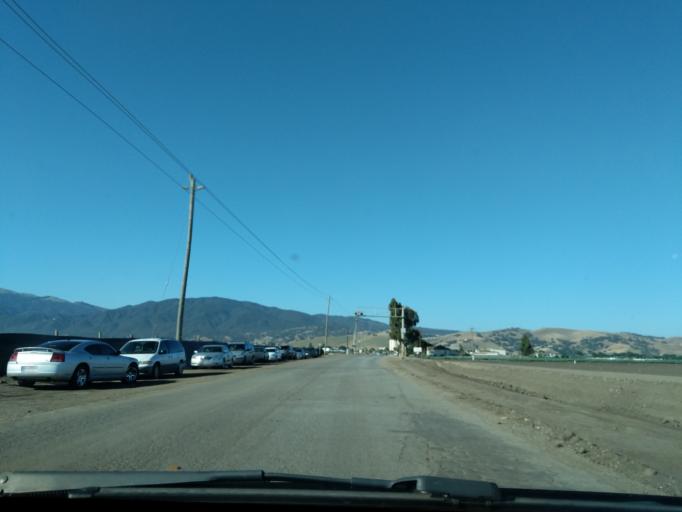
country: US
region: California
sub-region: Monterey County
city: Salinas
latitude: 36.6339
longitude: -121.6402
